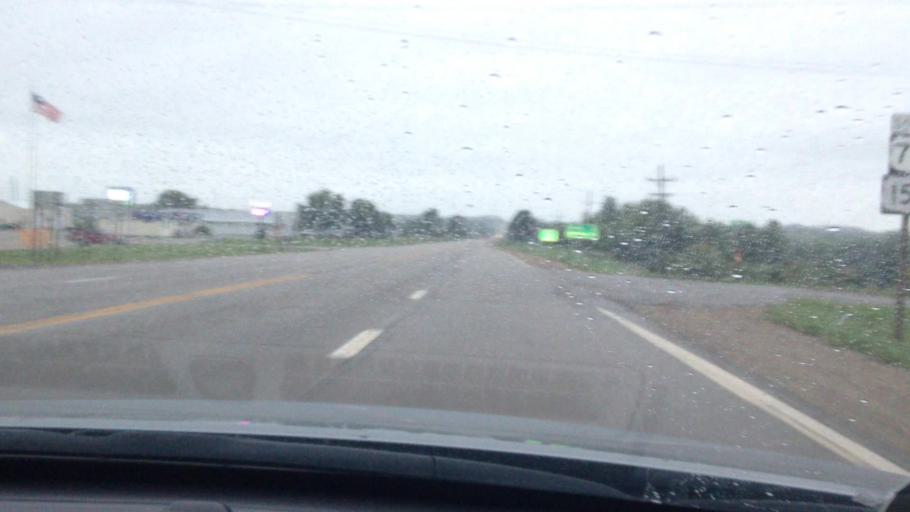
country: US
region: Kansas
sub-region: Brown County
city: Hiawatha
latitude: 39.8395
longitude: -95.5272
